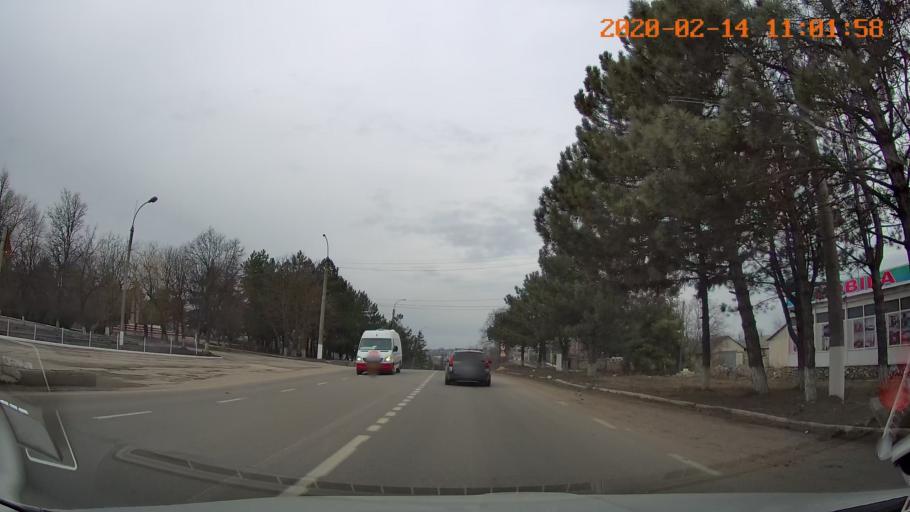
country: MD
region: Raionul Edinet
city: Edinet
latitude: 48.1626
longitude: 27.3242
